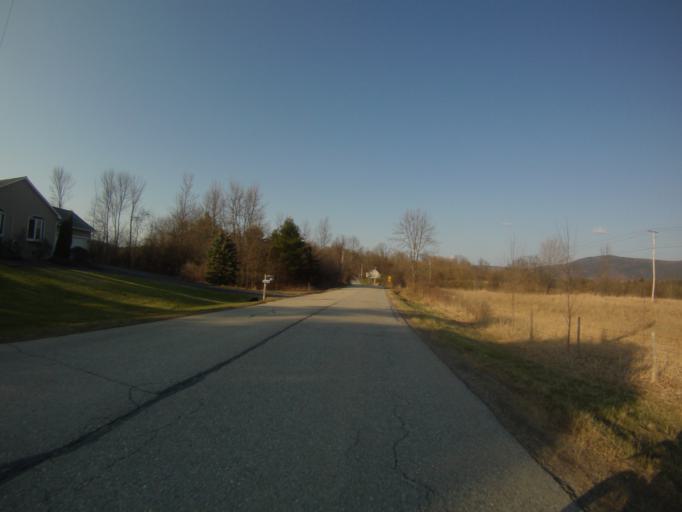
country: US
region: Vermont
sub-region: Addison County
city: Middlebury (village)
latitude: 44.0287
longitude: -73.1468
